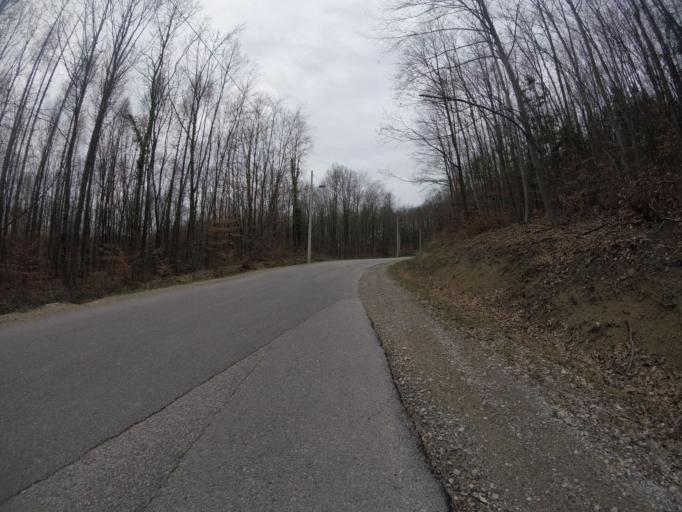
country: HR
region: Grad Zagreb
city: Strmec
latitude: 45.6372
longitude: 15.9342
